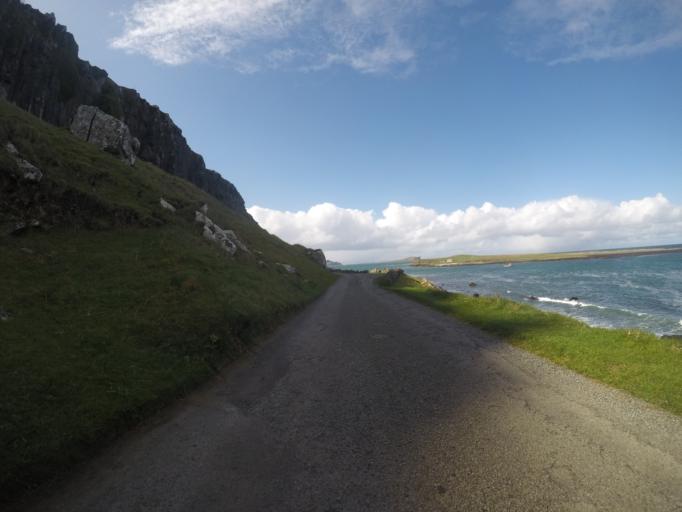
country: GB
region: Scotland
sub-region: Highland
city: Portree
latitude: 57.6355
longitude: -6.2039
